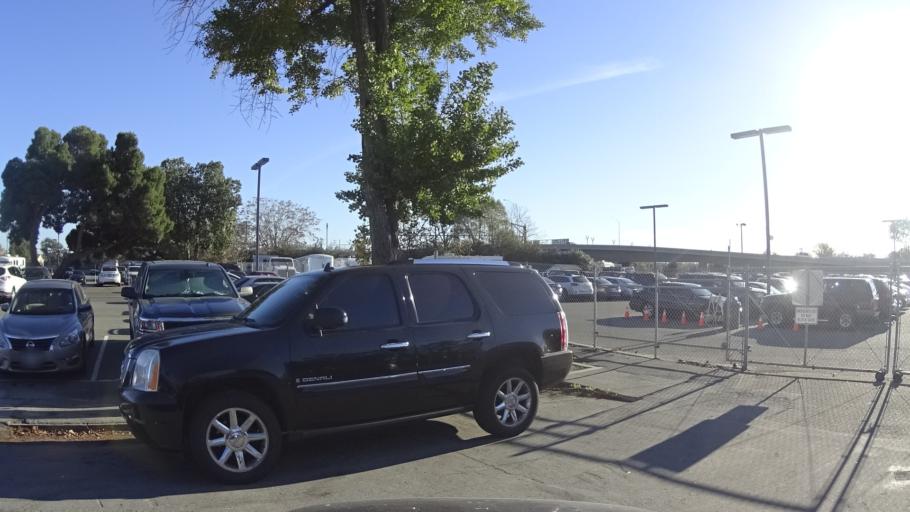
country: US
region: California
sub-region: Santa Clara County
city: San Jose
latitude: 37.3485
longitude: -121.9048
